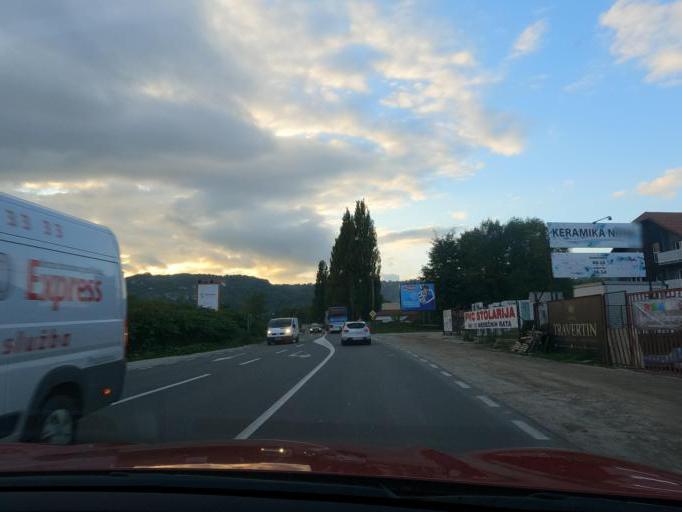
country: RS
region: Central Serbia
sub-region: Zlatiborski Okrug
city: Uzice
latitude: 43.8398
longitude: 19.8985
